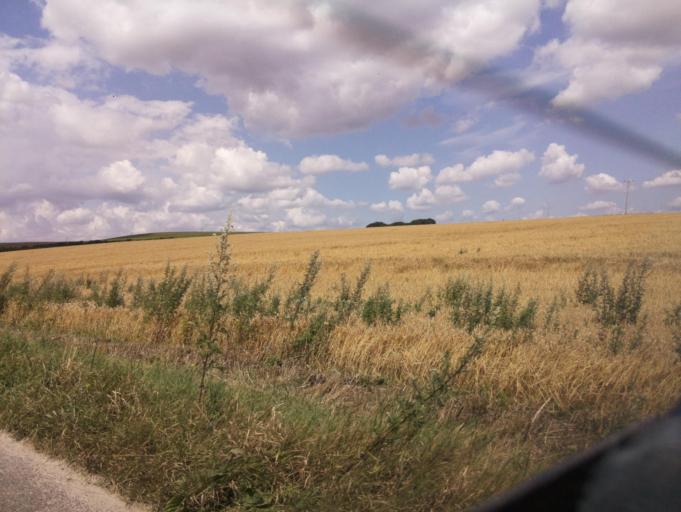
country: GB
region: England
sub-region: West Berkshire
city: Lambourn
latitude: 51.5231
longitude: -1.5771
